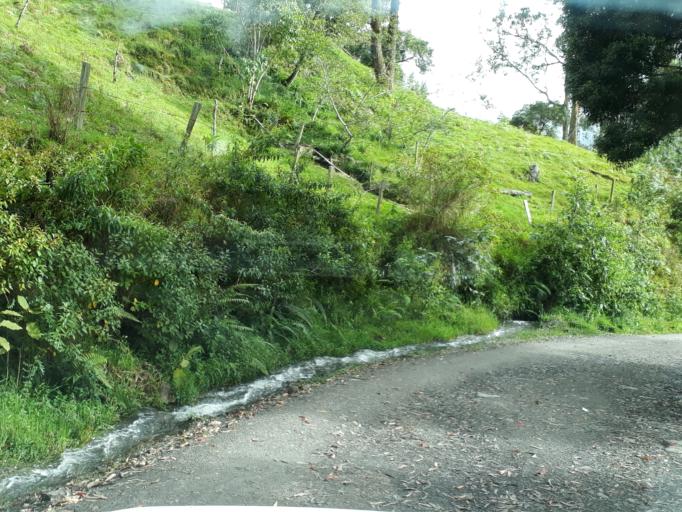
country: CO
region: Cundinamarca
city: Junin
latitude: 4.7843
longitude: -73.6882
